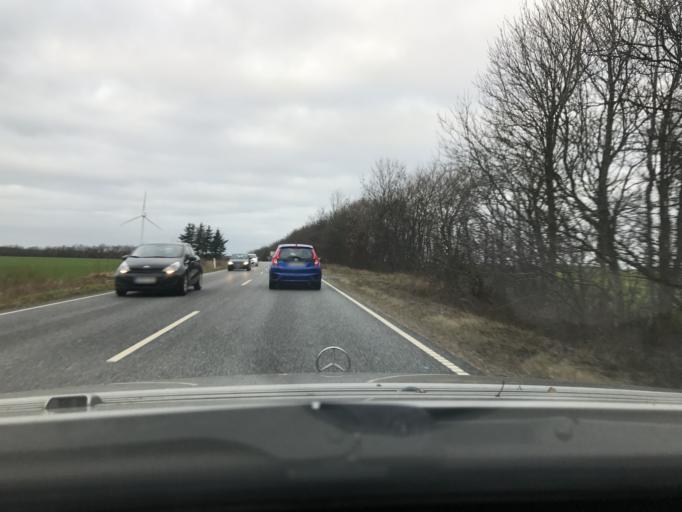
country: DK
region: South Denmark
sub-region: Aabenraa Kommune
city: Rodekro
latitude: 55.1059
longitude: 9.1831
